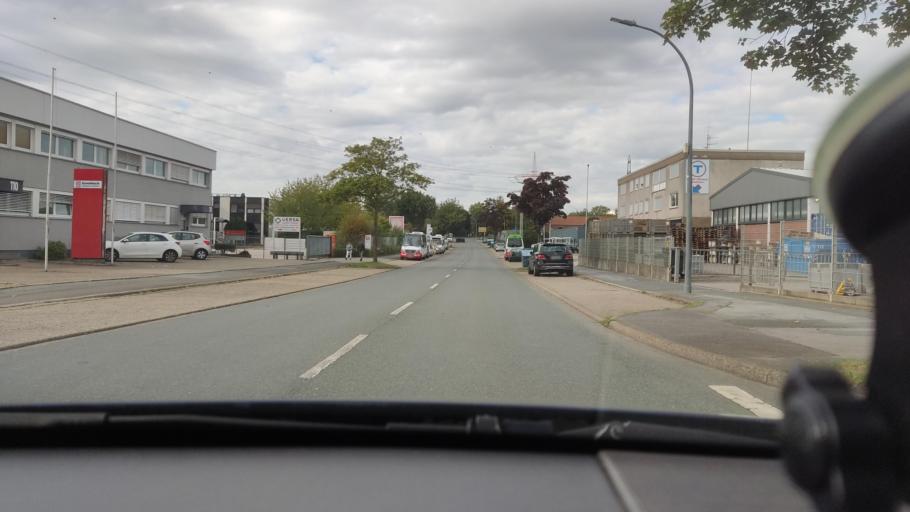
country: DE
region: North Rhine-Westphalia
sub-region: Regierungsbezirk Arnsberg
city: Dortmund
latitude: 51.5059
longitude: 7.3931
